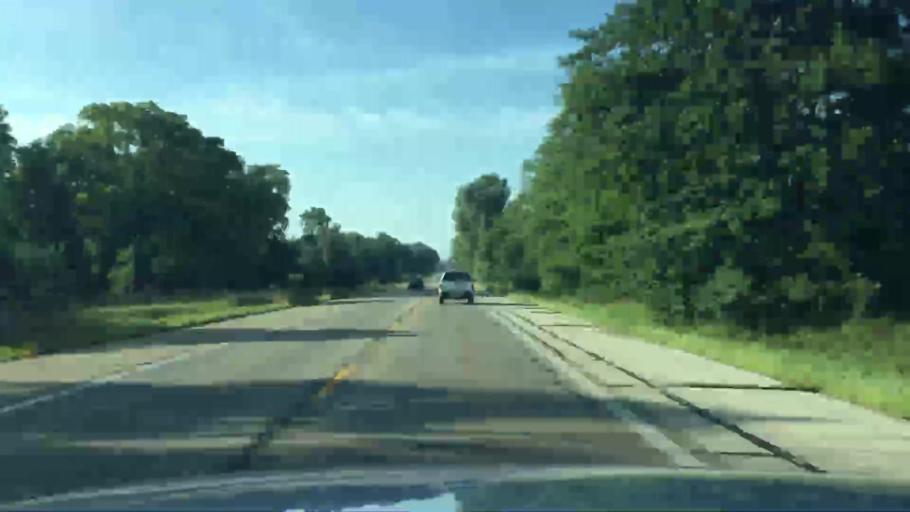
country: US
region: Michigan
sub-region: Jackson County
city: Vandercook Lake
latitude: 42.0986
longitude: -84.3639
